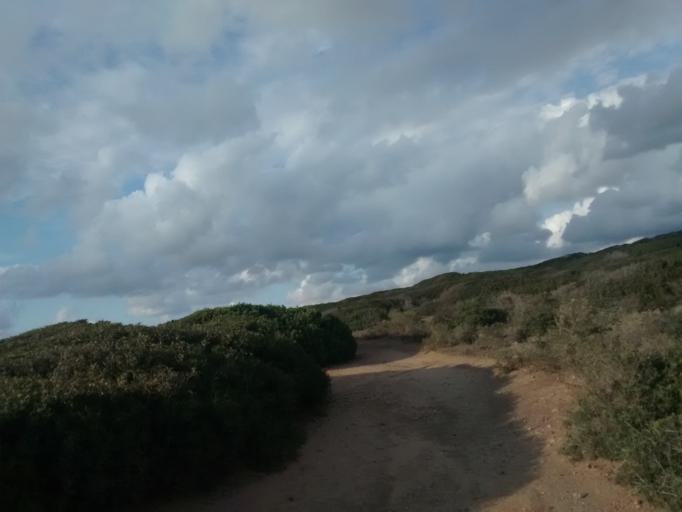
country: IT
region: Sardinia
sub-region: Provincia di Oristano
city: Narbolia
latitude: 40.0951
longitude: 8.4896
